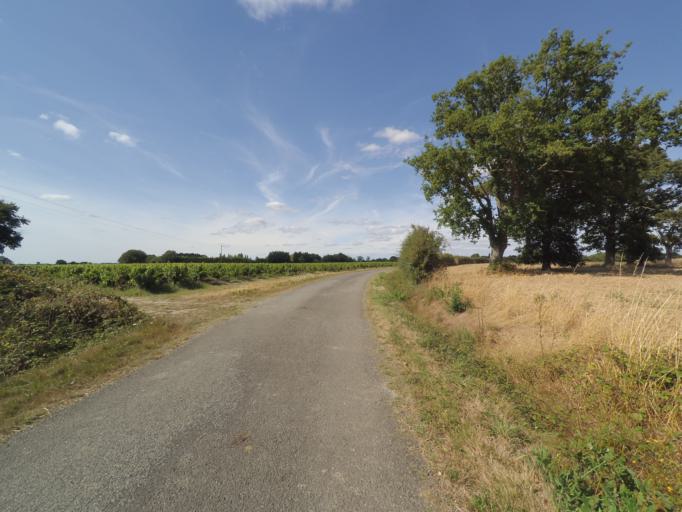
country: FR
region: Pays de la Loire
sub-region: Departement de la Loire-Atlantique
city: Vieillevigne
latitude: 46.9598
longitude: -1.4428
